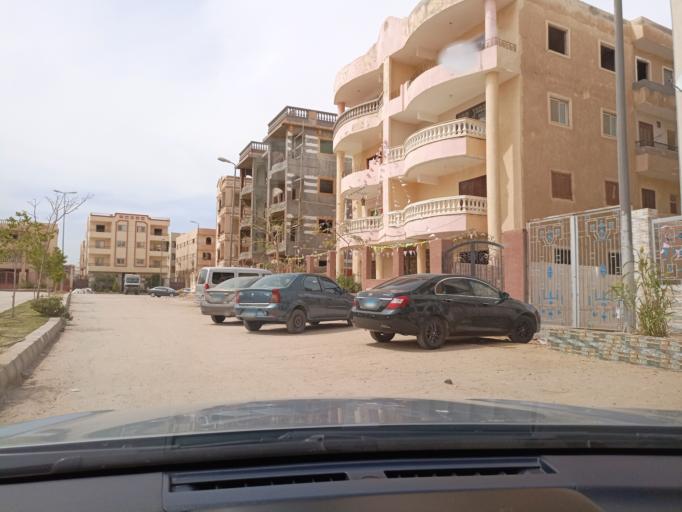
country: EG
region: Muhafazat al Qalyubiyah
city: Al Khankah
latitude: 30.2507
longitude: 31.5019
